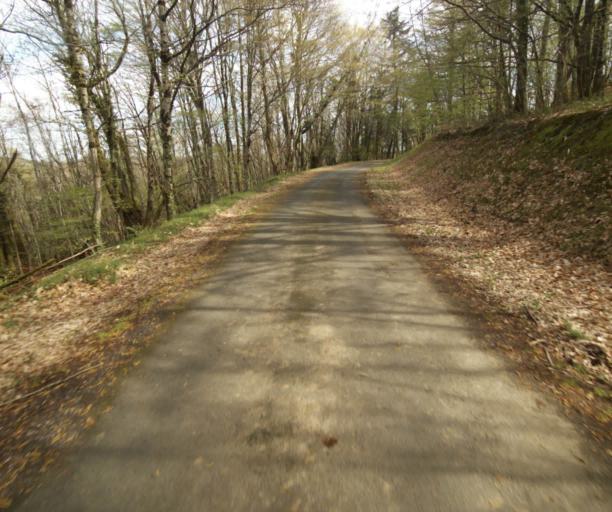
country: FR
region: Limousin
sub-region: Departement de la Correze
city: Laguenne
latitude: 45.2565
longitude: 1.8083
